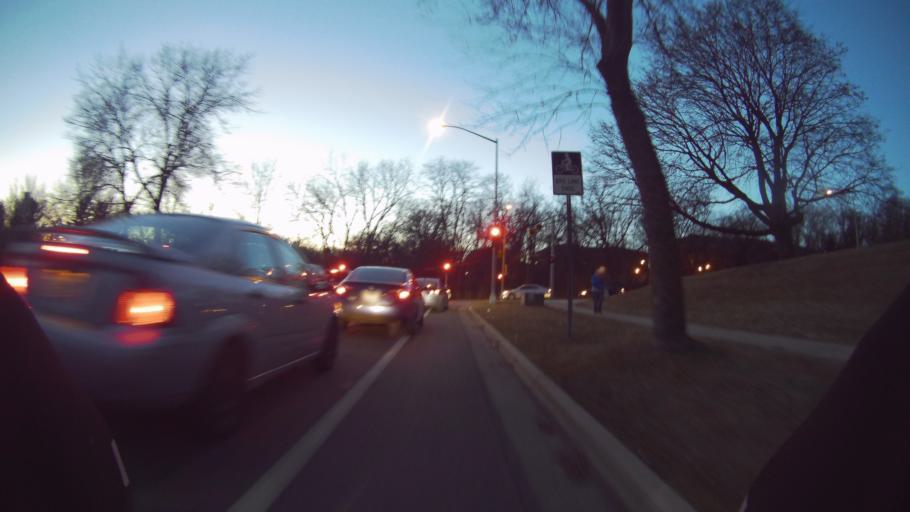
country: US
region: Wisconsin
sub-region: Dane County
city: Middleton
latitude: 43.0463
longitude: -89.5027
